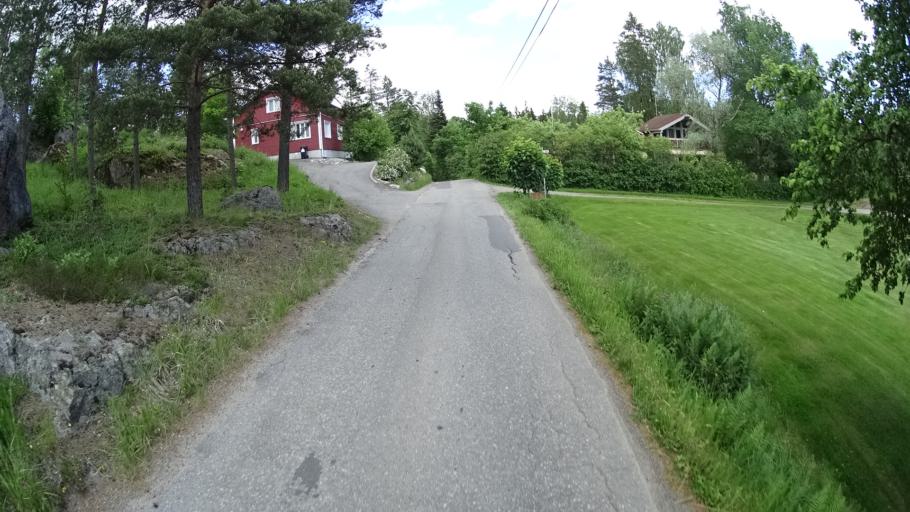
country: FI
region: Uusimaa
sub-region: Helsinki
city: Sibbo
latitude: 60.2581
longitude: 25.3117
